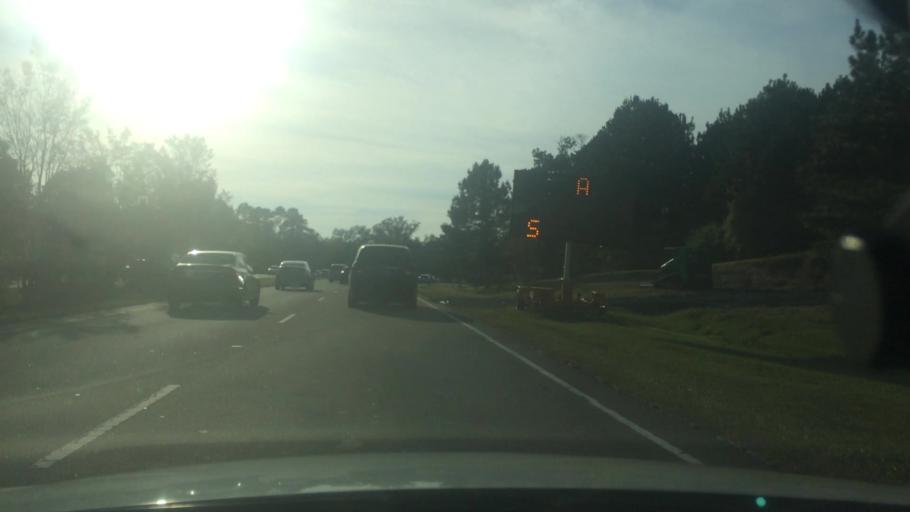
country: US
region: North Carolina
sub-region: Orange County
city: Chapel Hill
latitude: 35.9023
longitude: -79.0044
